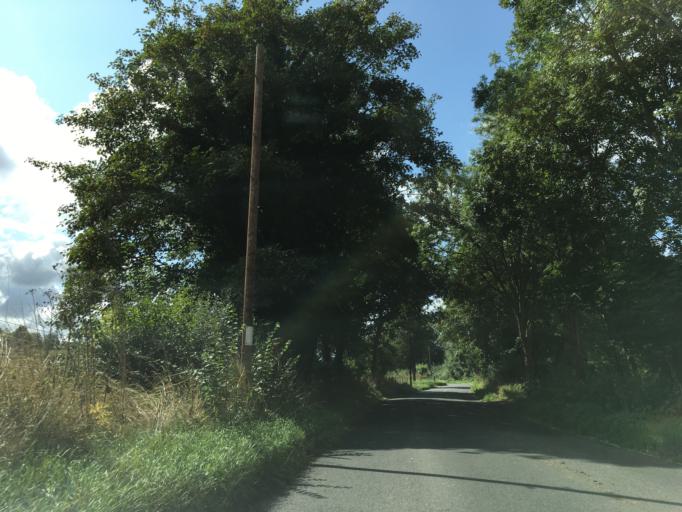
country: GB
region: England
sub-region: Hampshire
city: Kings Worthy
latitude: 51.1725
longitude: -1.3769
